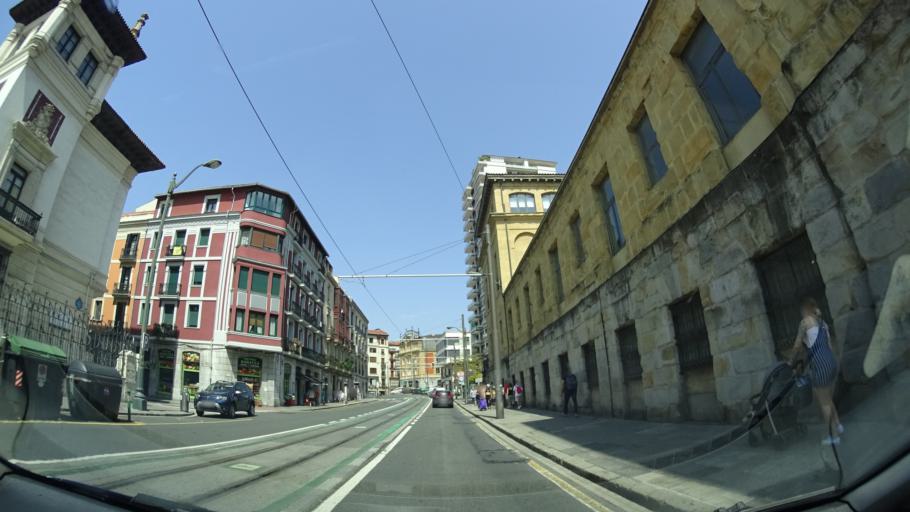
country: ES
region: Basque Country
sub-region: Bizkaia
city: Santutxu
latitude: 43.2547
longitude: -2.9218
